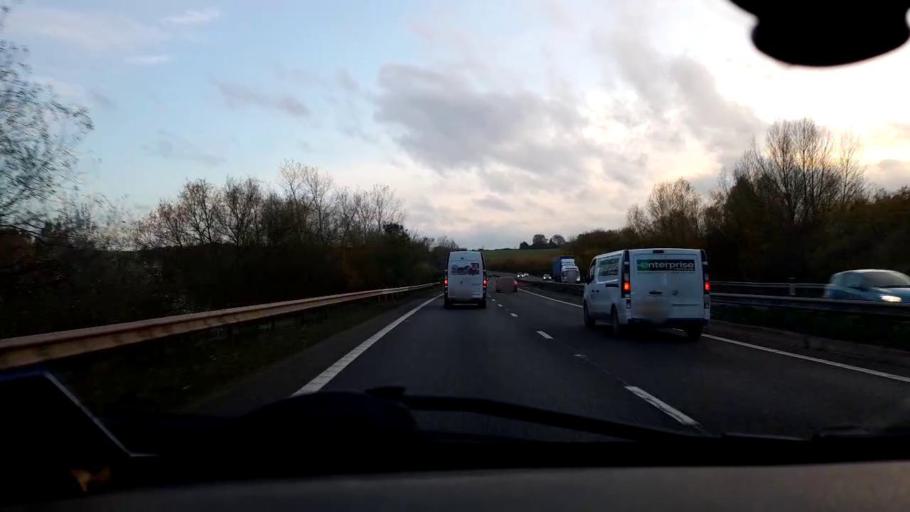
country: GB
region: England
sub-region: Norfolk
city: Bowthorpe
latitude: 52.6339
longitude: 1.1960
